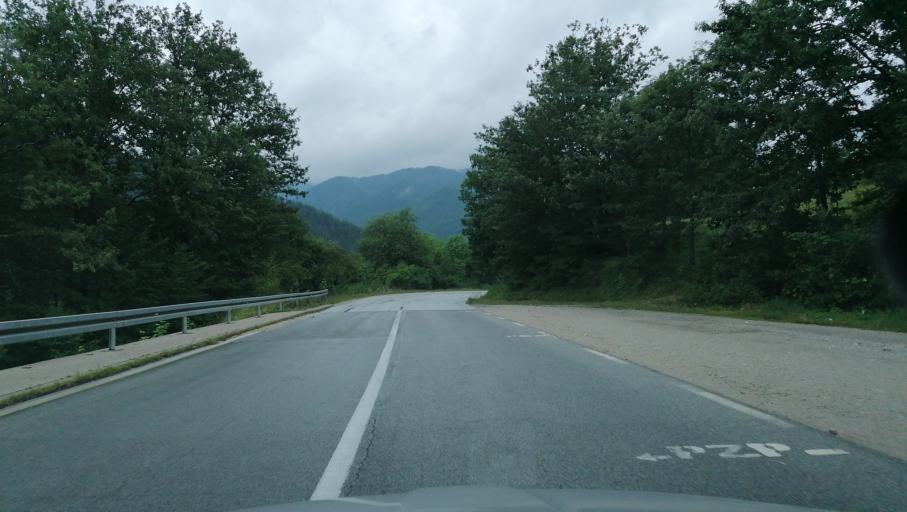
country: RS
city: Durici
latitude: 43.8055
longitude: 19.5111
